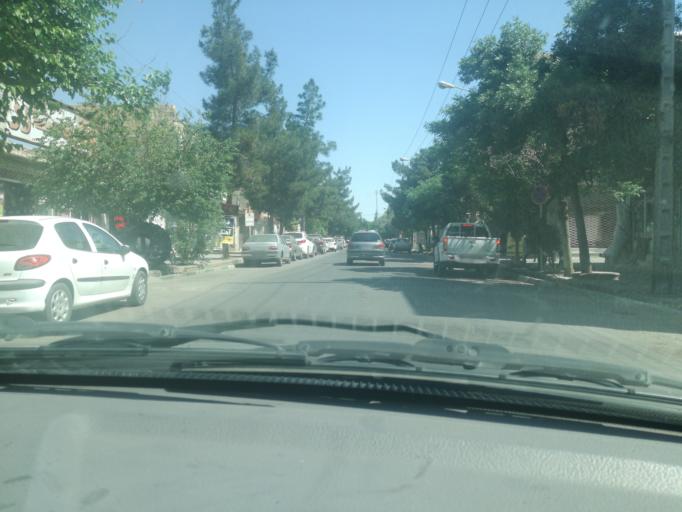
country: IR
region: Razavi Khorasan
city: Sarakhs
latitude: 36.5403
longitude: 61.1637
